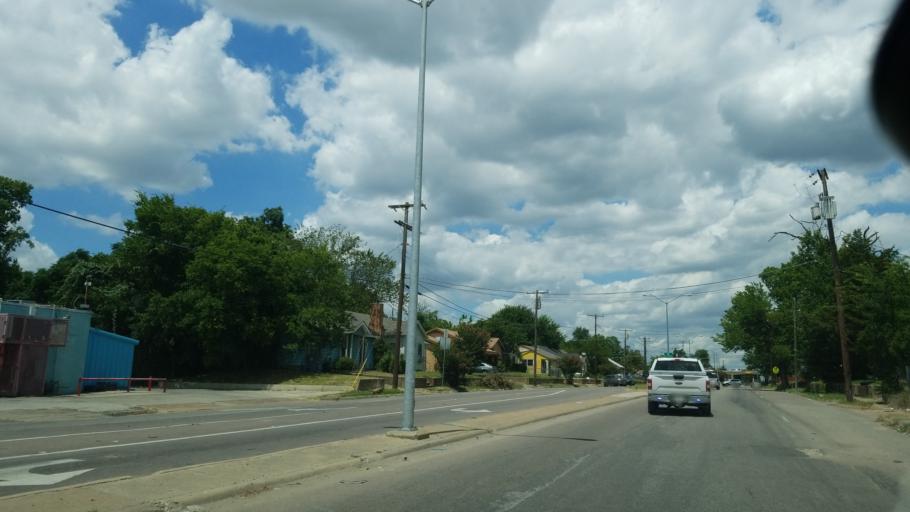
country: US
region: Texas
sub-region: Dallas County
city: Dallas
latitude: 32.7474
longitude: -96.7637
